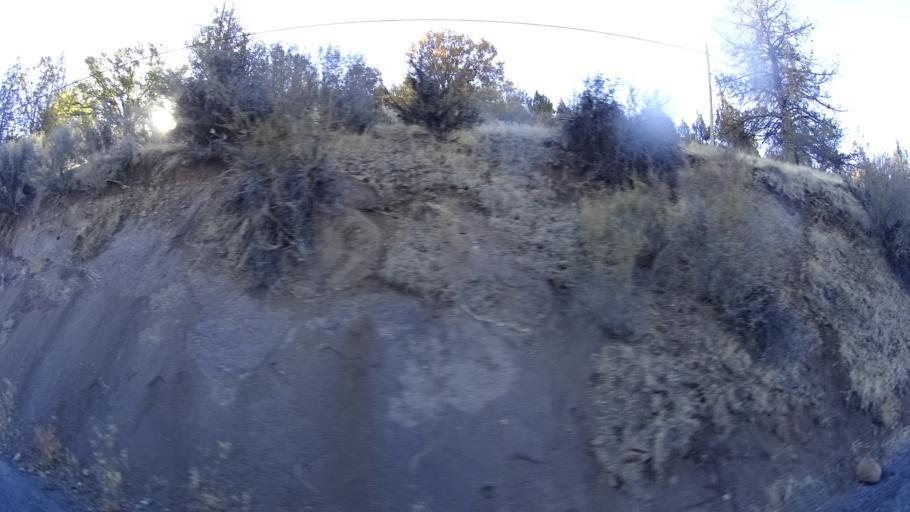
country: US
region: California
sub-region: Siskiyou County
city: Montague
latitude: 41.9431
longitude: -122.4413
